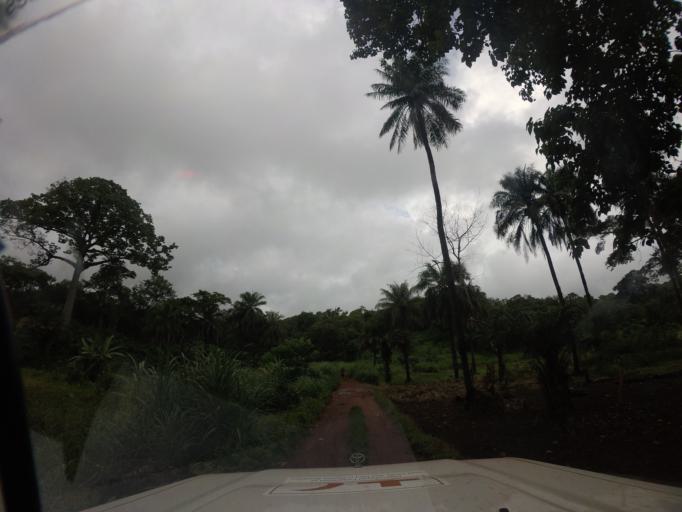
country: SL
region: Northern Province
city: Kamakwie
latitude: 9.6750
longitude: -12.2222
